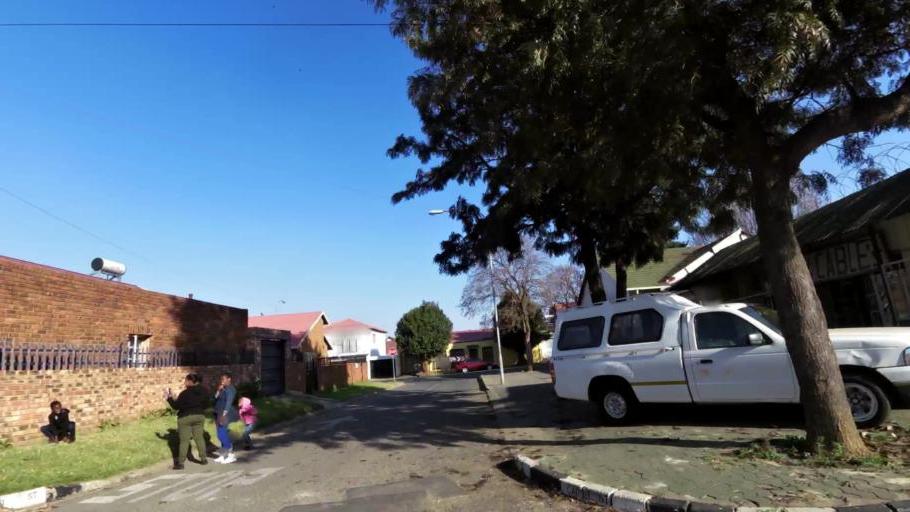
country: ZA
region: Gauteng
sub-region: City of Johannesburg Metropolitan Municipality
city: Johannesburg
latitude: -26.1930
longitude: 28.0165
